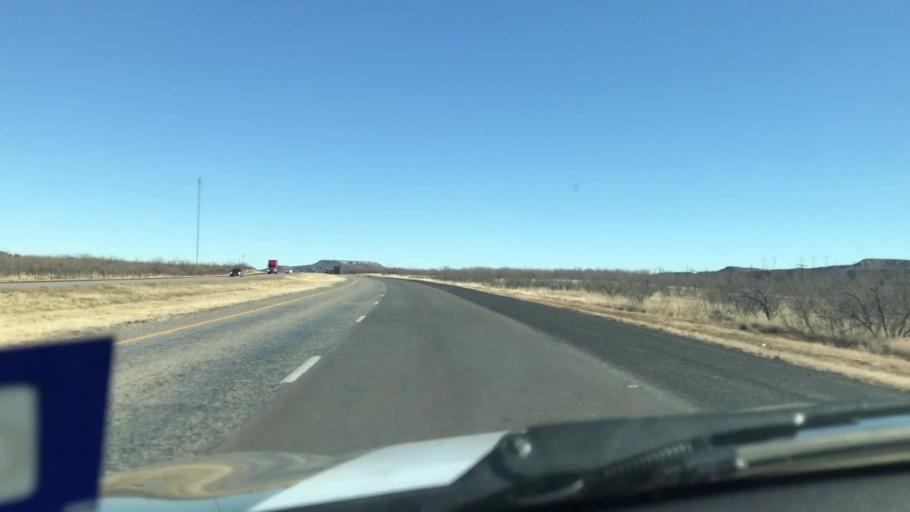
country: US
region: Texas
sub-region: Garza County
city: Post
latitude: 32.9879
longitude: -101.1368
